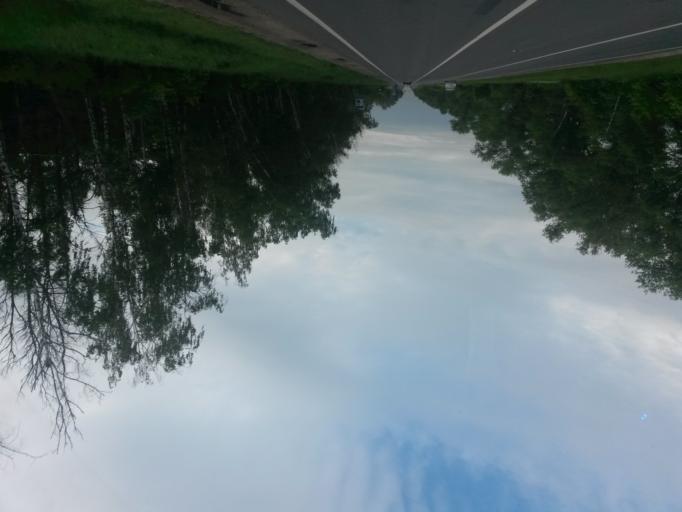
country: RU
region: Moskovskaya
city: Belyye Stolby
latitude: 55.3288
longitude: 37.8053
